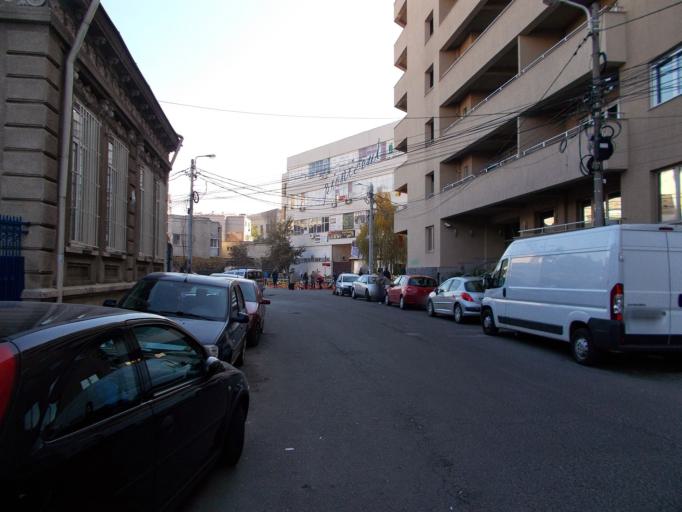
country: RO
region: Bucuresti
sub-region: Municipiul Bucuresti
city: Bucharest
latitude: 44.4213
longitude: 26.1068
